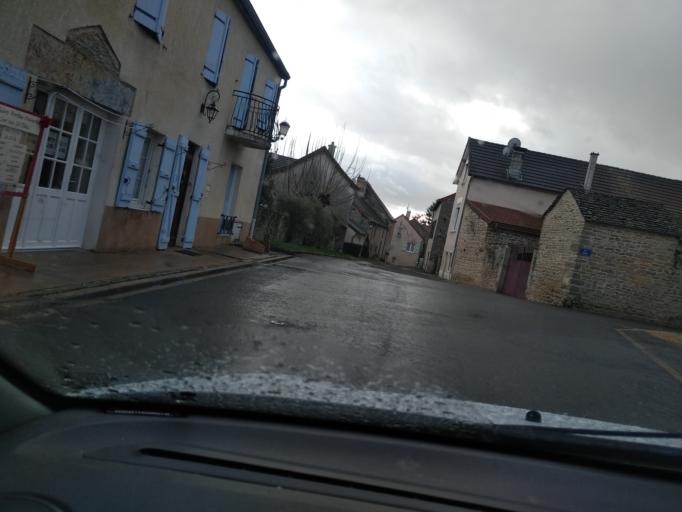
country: FR
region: Bourgogne
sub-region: Departement de Saone-et-Loire
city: Saint-Leger-sur-Dheune
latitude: 46.8678
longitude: 4.6846
